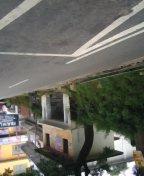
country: IN
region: Himachal Pradesh
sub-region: Kangra
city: Dharmsala
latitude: 32.2064
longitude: 76.3242
